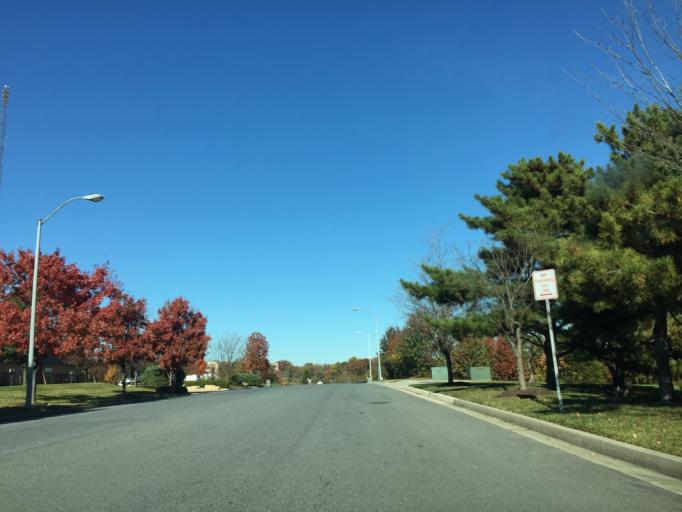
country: US
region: Maryland
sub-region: Baltimore County
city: Lansdowne
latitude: 39.2524
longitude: -76.6738
